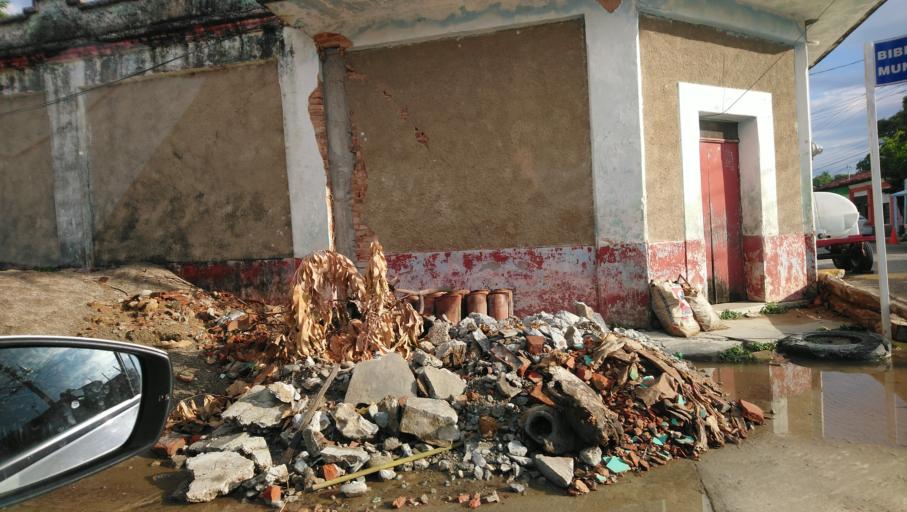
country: MX
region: Oaxaca
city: San Pedro Tapanatepec
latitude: 16.3668
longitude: -94.1900
